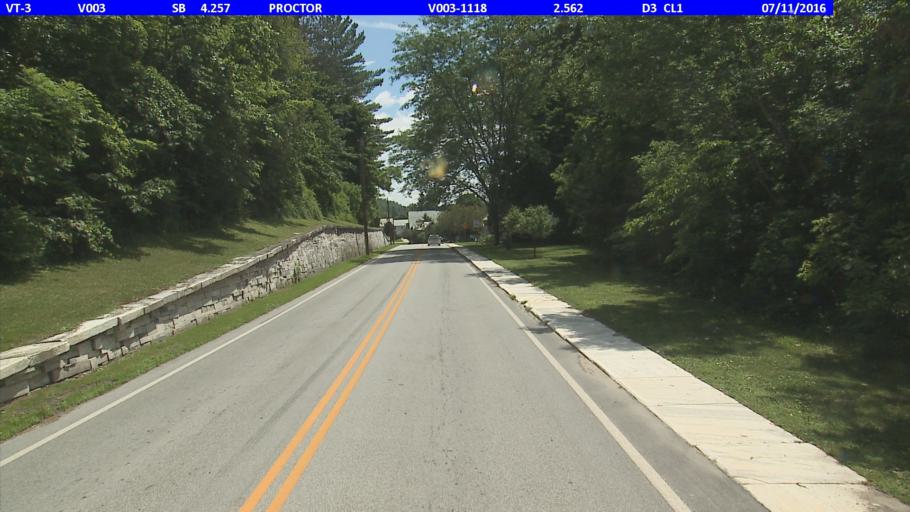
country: US
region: Vermont
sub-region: Rutland County
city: West Rutland
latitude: 43.6607
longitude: -73.0325
